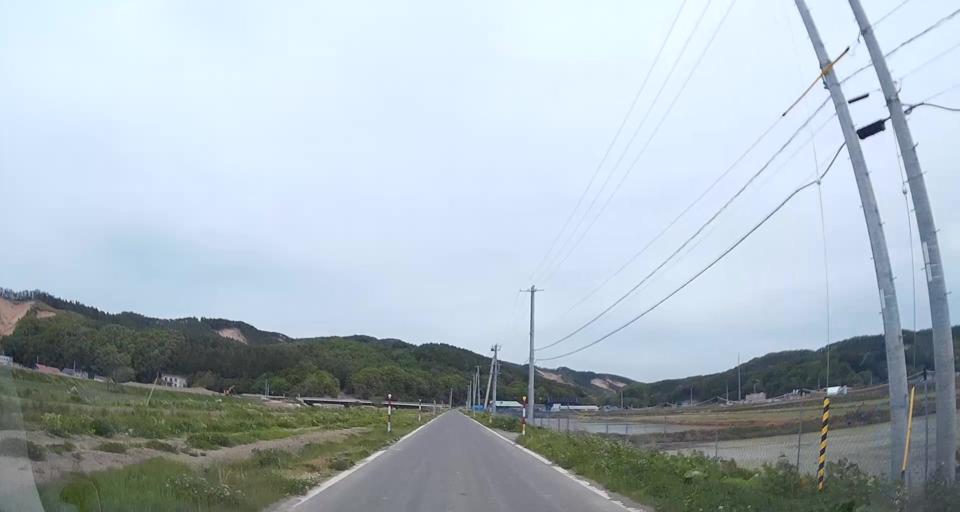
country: JP
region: Hokkaido
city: Chitose
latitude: 42.7537
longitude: 141.9709
